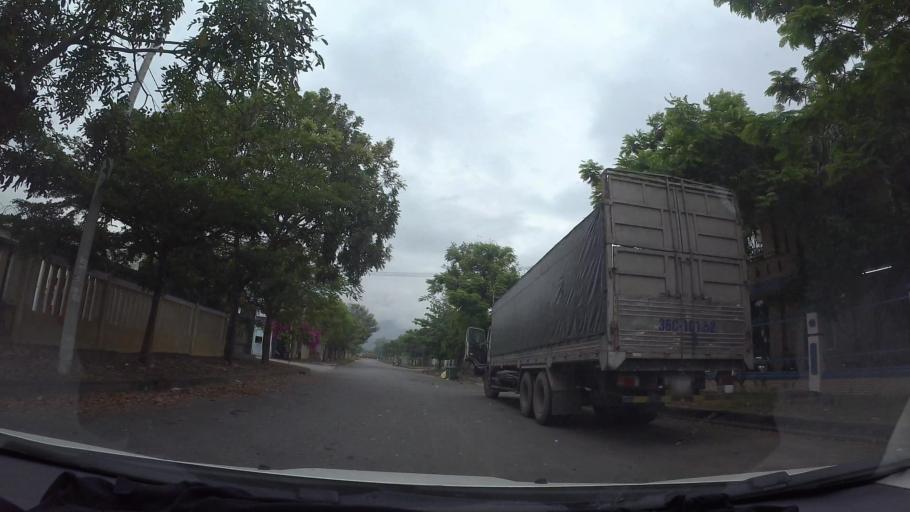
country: VN
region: Da Nang
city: Lien Chieu
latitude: 16.1254
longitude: 108.1173
